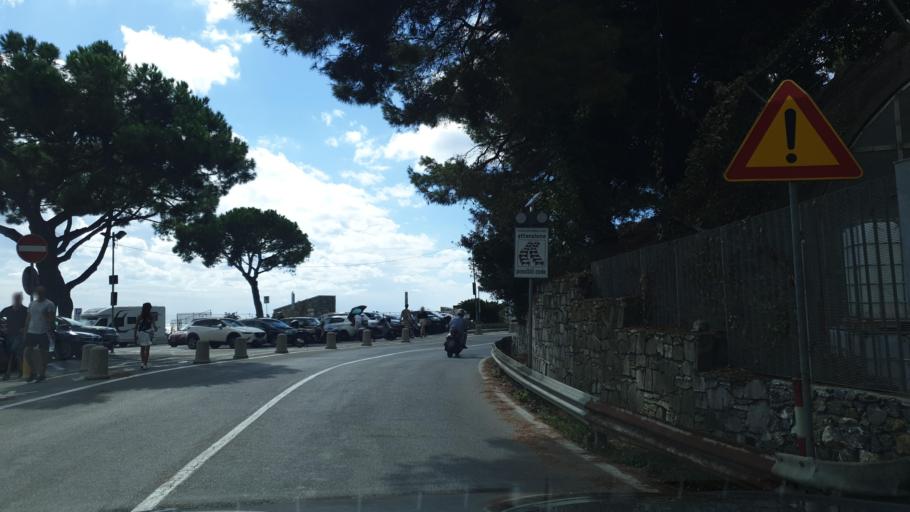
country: IT
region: Liguria
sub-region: Provincia di Genova
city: Santa Margherita Ligure
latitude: 44.3228
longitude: 9.2157
